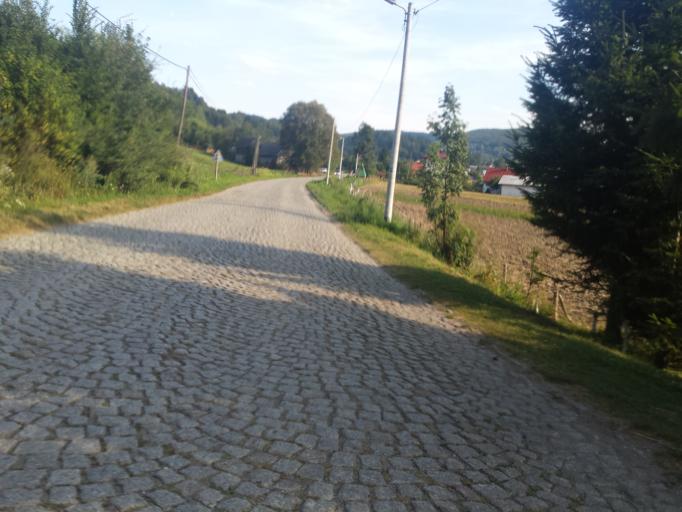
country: PL
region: Subcarpathian Voivodeship
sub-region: Powiat leski
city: Uherce Mineralne
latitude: 49.4421
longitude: 22.4081
